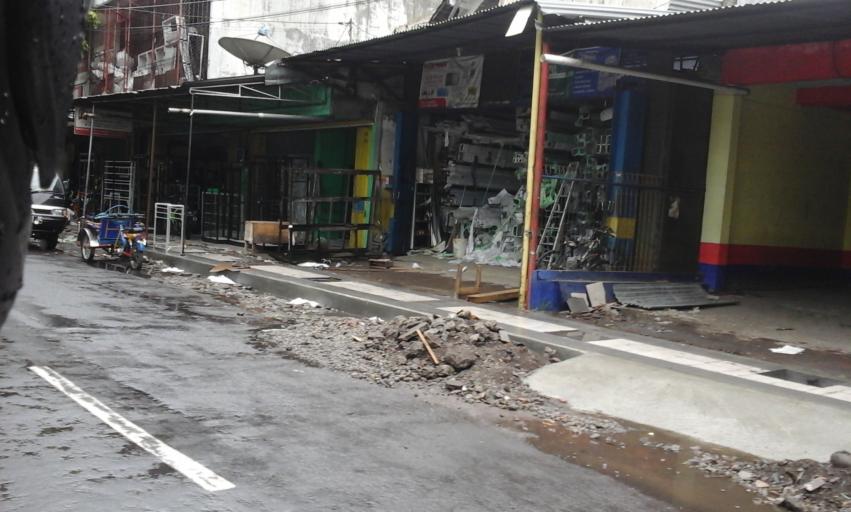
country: ID
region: East Java
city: Kadipaten
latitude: -8.1301
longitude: 113.2158
